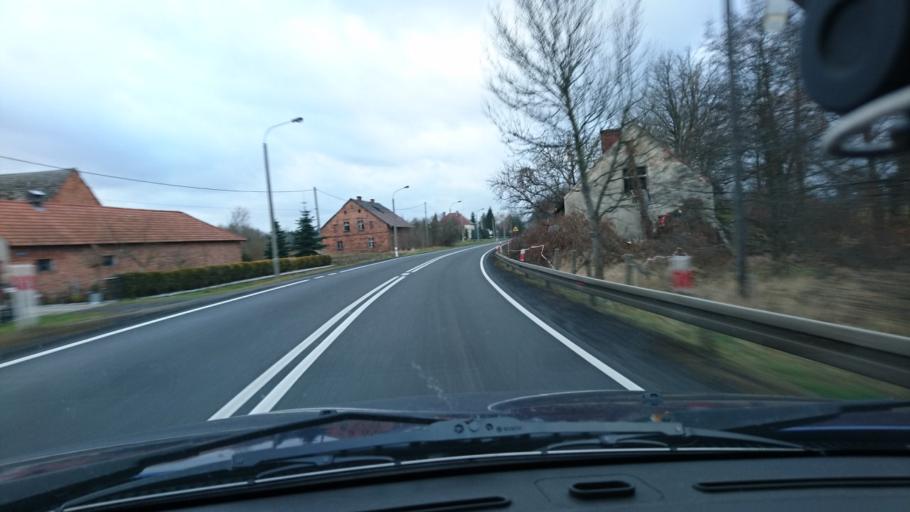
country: PL
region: Opole Voivodeship
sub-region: Powiat oleski
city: Olesno
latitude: 50.9131
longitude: 18.3494
